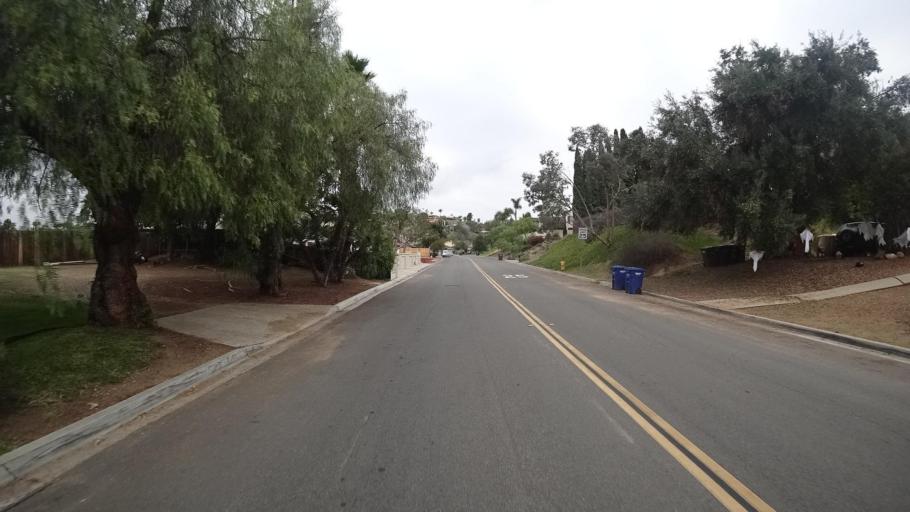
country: US
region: California
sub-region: San Diego County
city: Spring Valley
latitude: 32.7593
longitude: -116.9920
